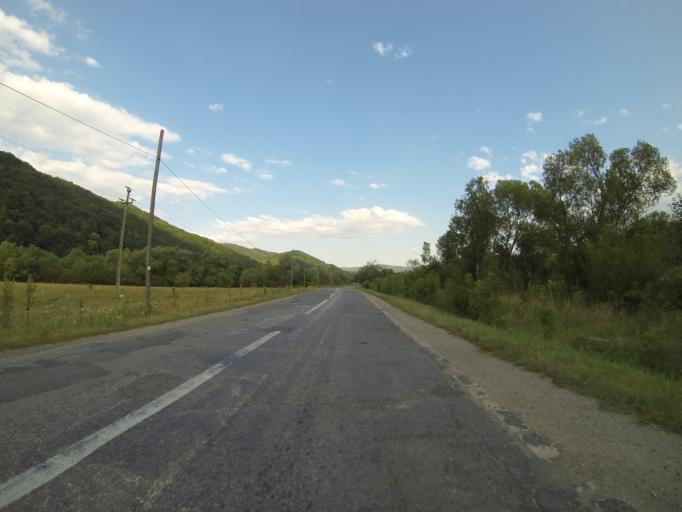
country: RO
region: Brasov
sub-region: Comuna Sinca Veche
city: Persani
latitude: 45.7389
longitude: 25.2234
